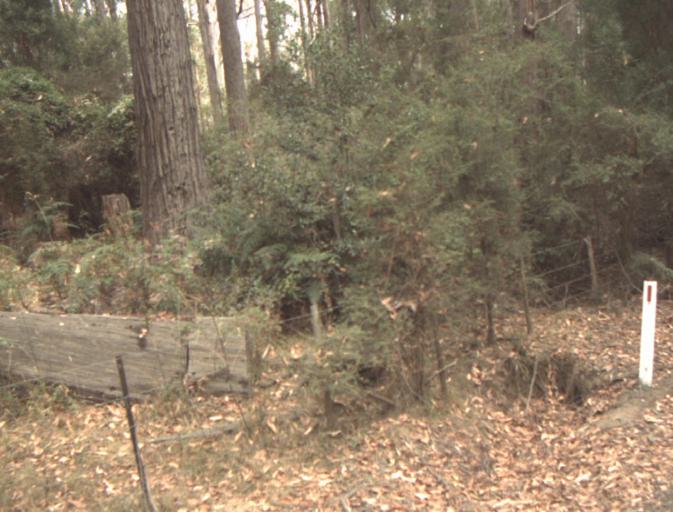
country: AU
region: Tasmania
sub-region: Launceston
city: Mayfield
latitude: -41.2706
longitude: 147.1795
